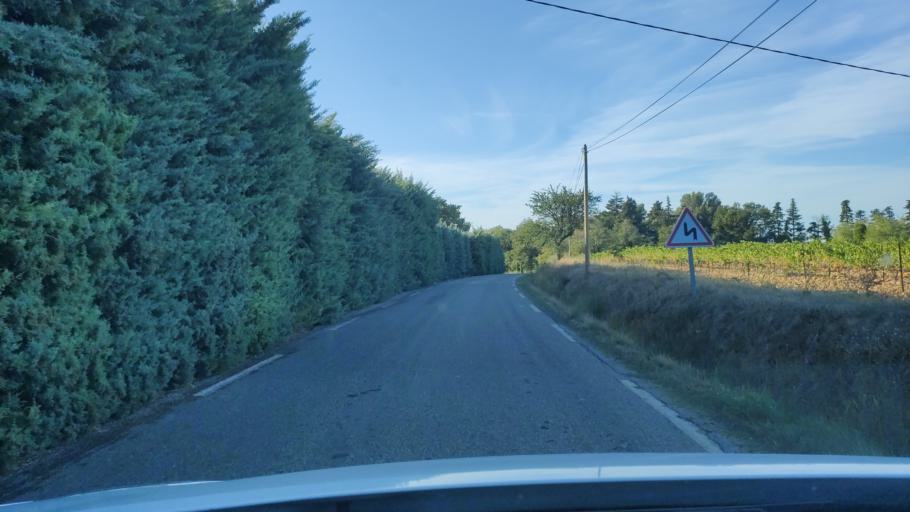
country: FR
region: Languedoc-Roussillon
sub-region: Departement du Gard
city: Saze
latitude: 43.9530
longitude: 4.6564
